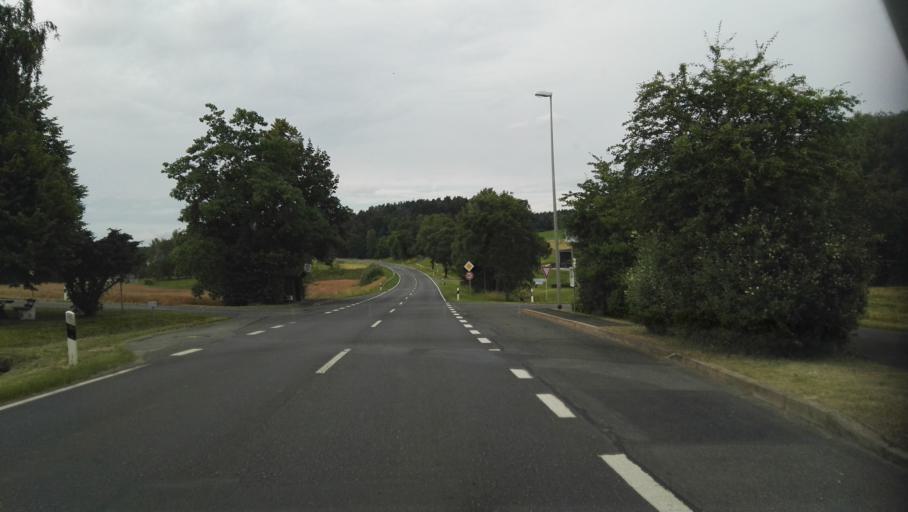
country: DE
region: Bavaria
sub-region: Upper Franconia
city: Plankenfels
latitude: 49.8958
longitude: 11.3333
